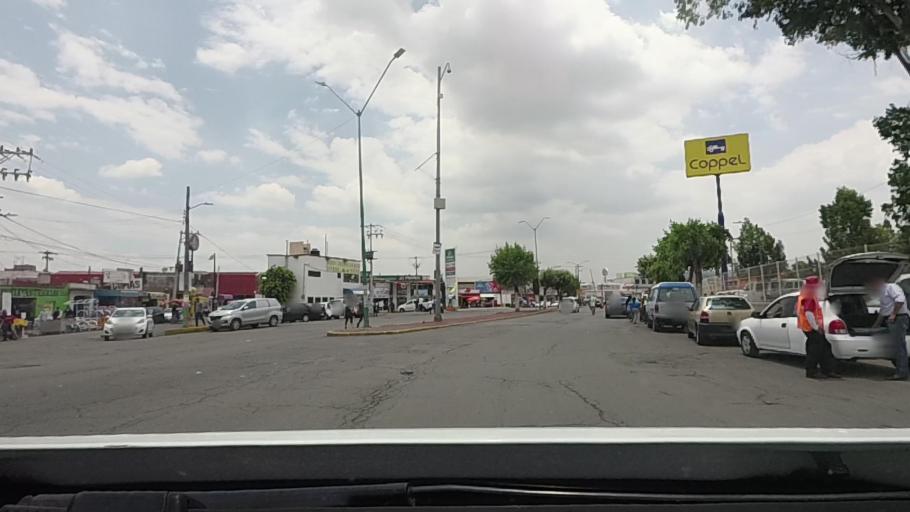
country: MX
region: Mexico
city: Chalco de Diaz Covarrubias
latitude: 19.2624
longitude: -98.8996
